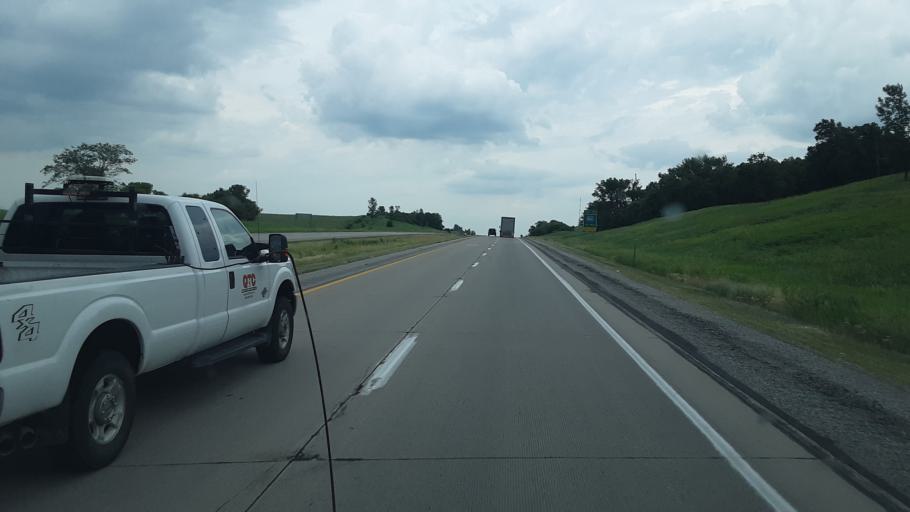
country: US
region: Iowa
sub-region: Pottawattamie County
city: Avoca
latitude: 41.4796
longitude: -95.5886
